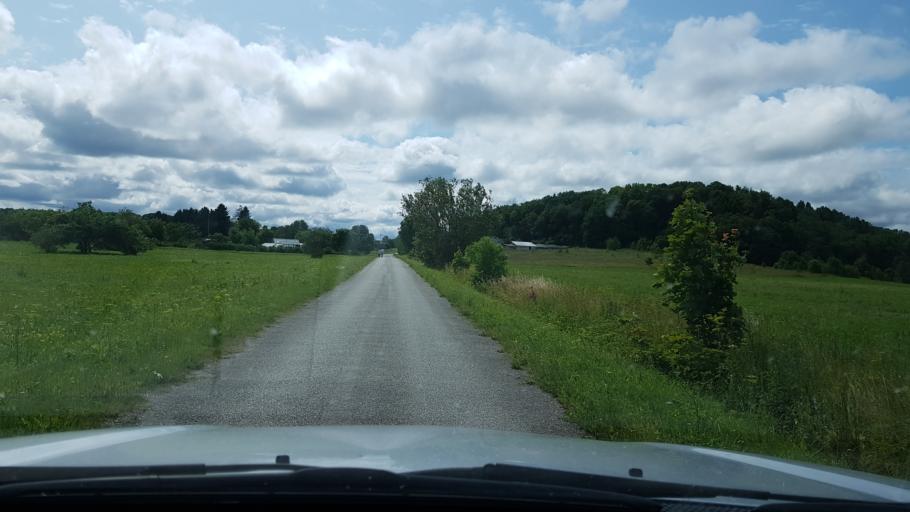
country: EE
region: Ida-Virumaa
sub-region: Sillamaee linn
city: Sillamae
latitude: 59.3774
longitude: 27.8725
